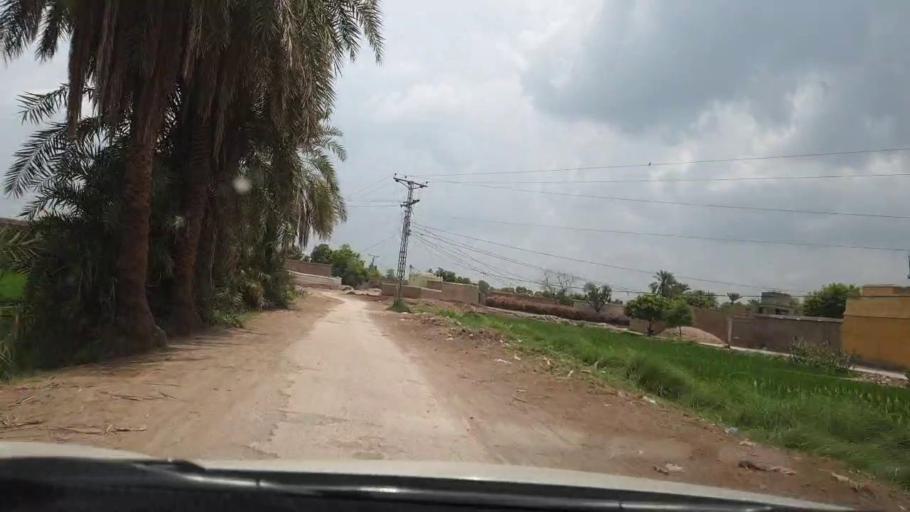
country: PK
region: Sindh
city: Goth Garelo
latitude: 27.4208
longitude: 68.1152
